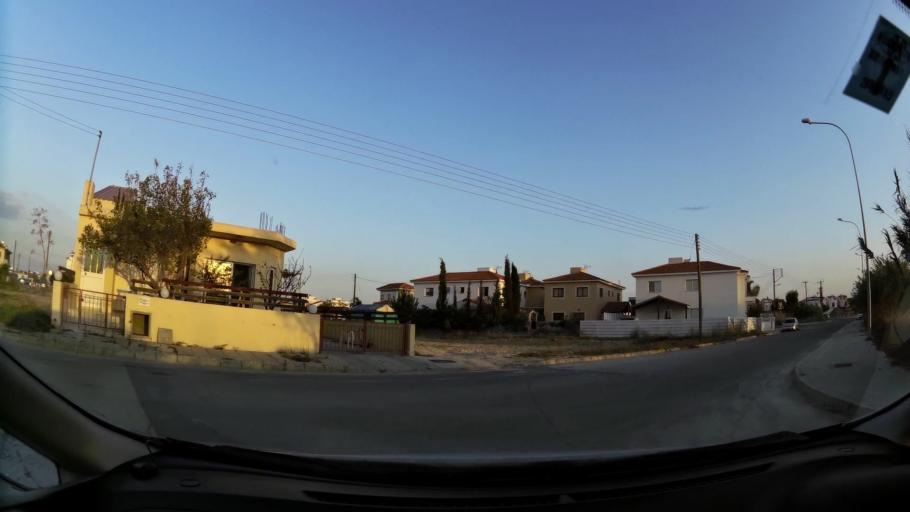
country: CY
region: Larnaka
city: Aradippou
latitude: 34.9173
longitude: 33.5836
